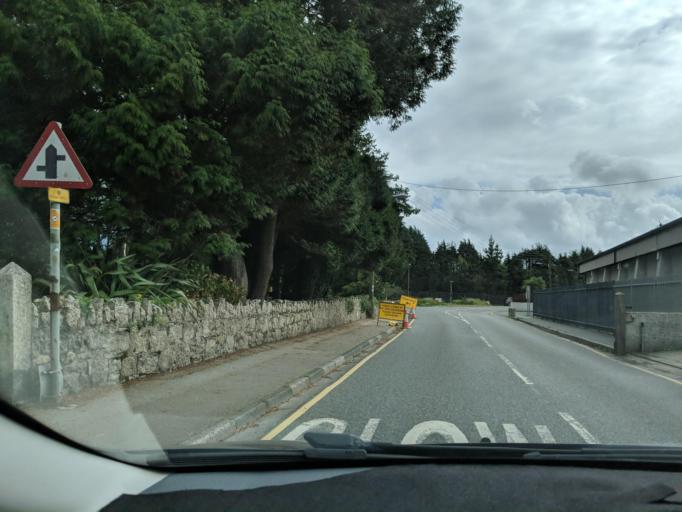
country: GB
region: England
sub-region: Cornwall
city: Par
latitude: 50.3580
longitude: -4.7126
